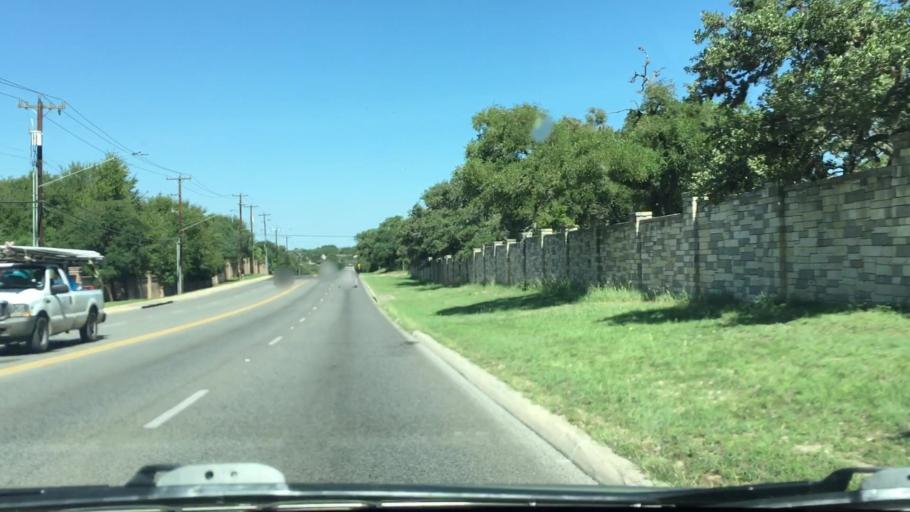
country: US
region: Texas
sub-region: Bexar County
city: Hollywood Park
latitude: 29.5767
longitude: -98.4974
